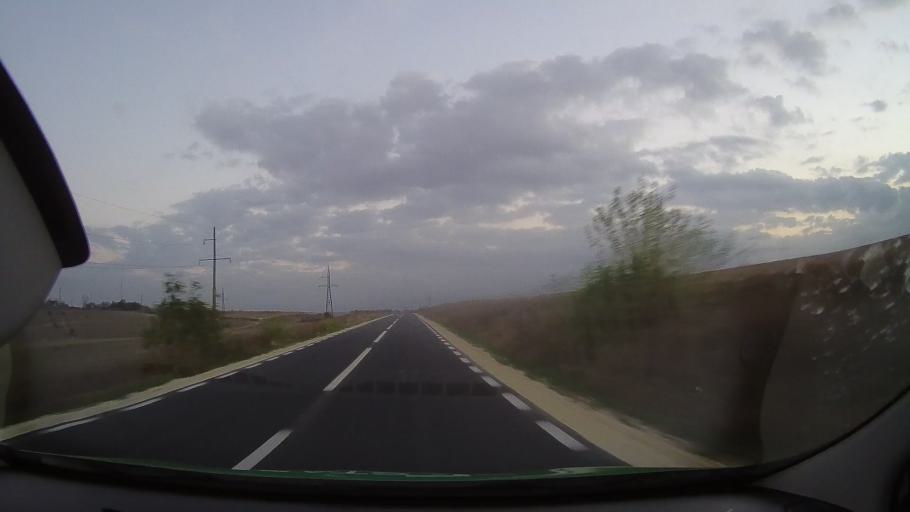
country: RO
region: Constanta
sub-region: Comuna Baneasa
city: Baneasa
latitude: 44.0835
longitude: 27.6885
